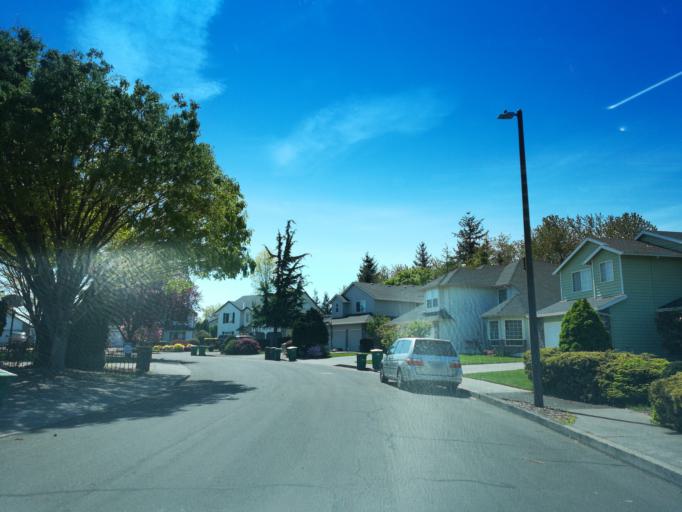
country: US
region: Oregon
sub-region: Multnomah County
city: Troutdale
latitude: 45.5253
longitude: -122.3940
